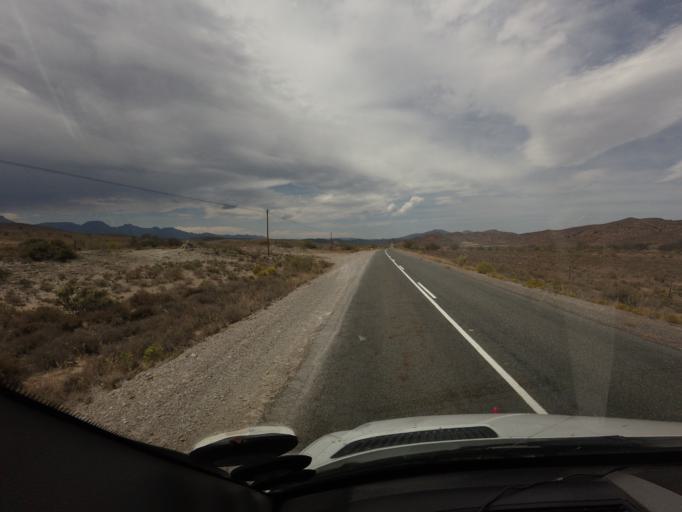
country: ZA
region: Western Cape
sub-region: Eden District Municipality
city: Ladismith
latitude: -33.5996
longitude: 21.0964
